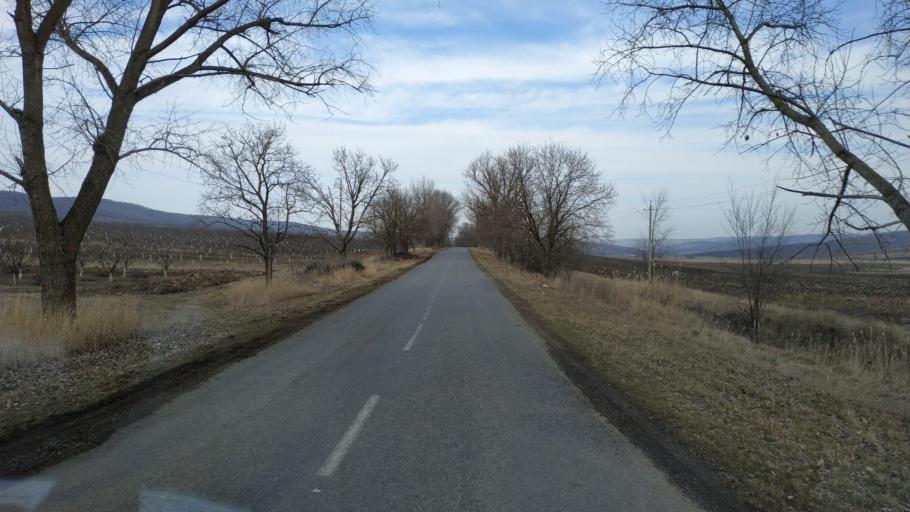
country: MD
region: Nisporeni
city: Nisporeni
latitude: 47.0975
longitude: 28.1314
